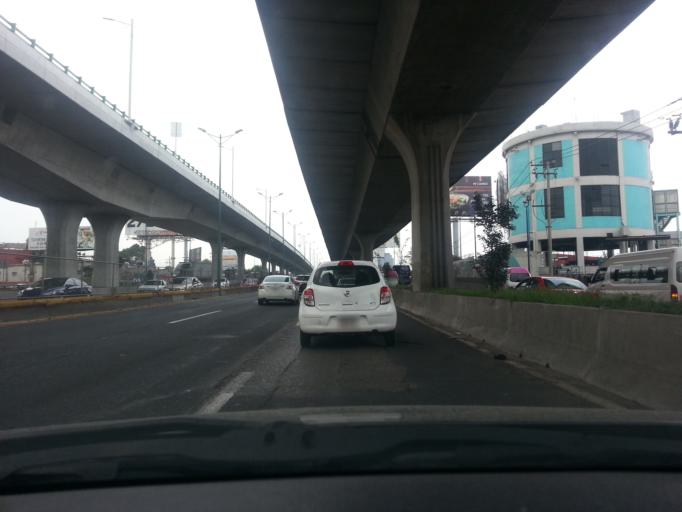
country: MX
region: Mexico
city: Naucalpan de Juarez
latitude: 19.4719
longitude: -99.2278
